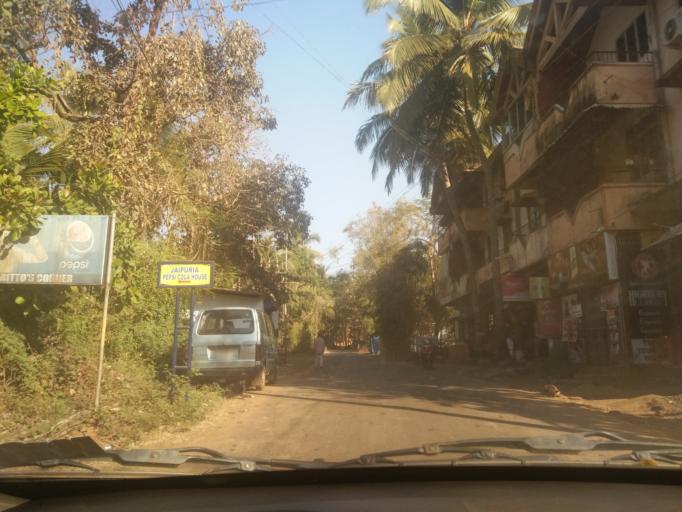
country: IN
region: Goa
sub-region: South Goa
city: Colva
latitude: 15.3077
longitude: 73.9120
